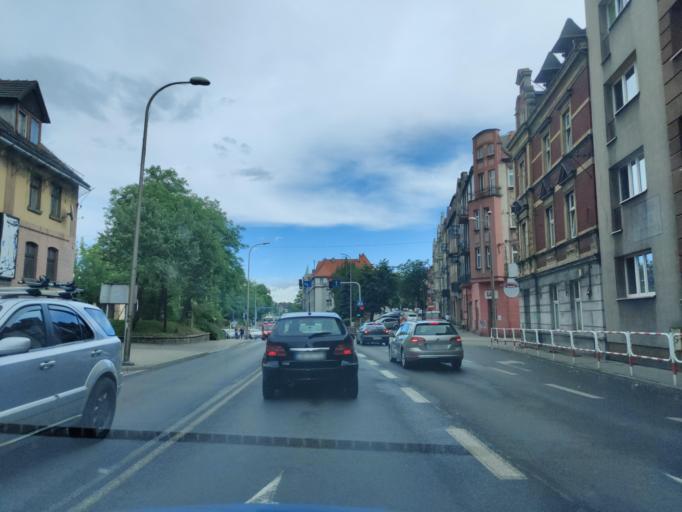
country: PL
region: Silesian Voivodeship
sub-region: Myslowice
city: Myslowice
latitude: 50.2420
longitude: 19.1357
